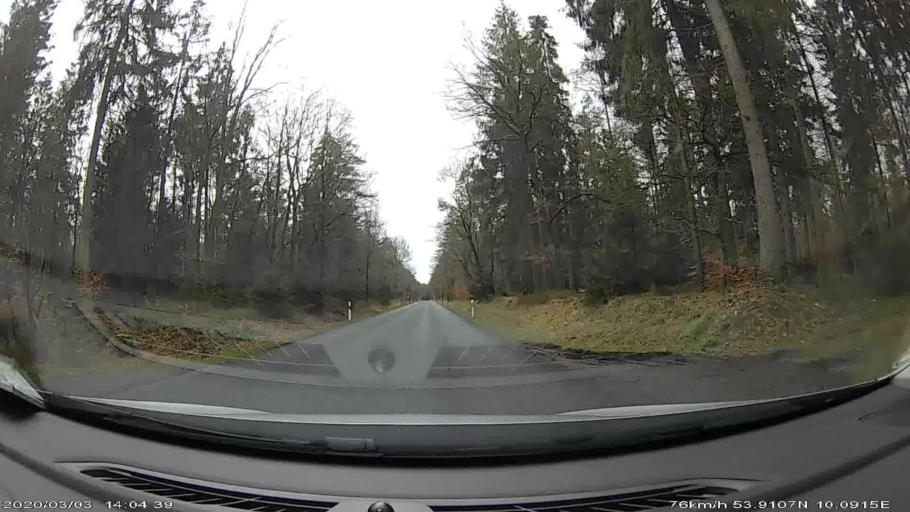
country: DE
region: Schleswig-Holstein
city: Hartenholm
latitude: 53.9100
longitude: 10.0910
